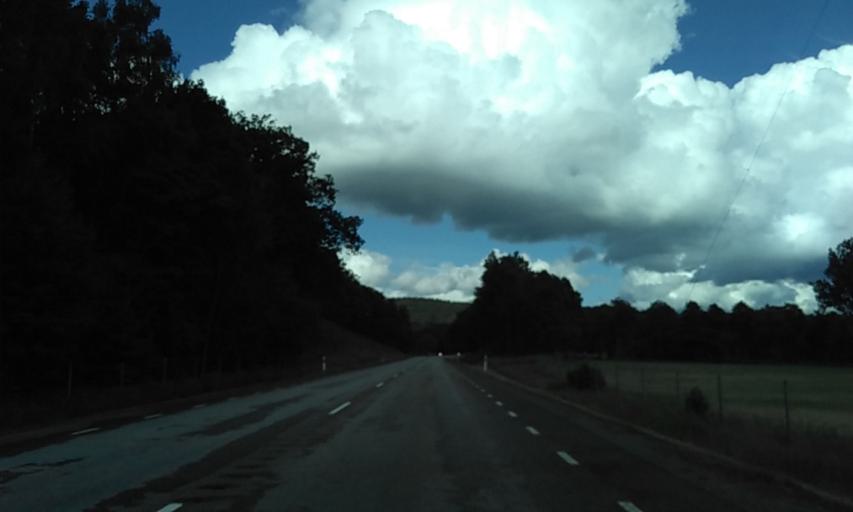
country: SE
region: Vaestra Goetaland
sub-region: Alingsas Kommun
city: Ingared
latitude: 57.9574
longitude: 12.3974
